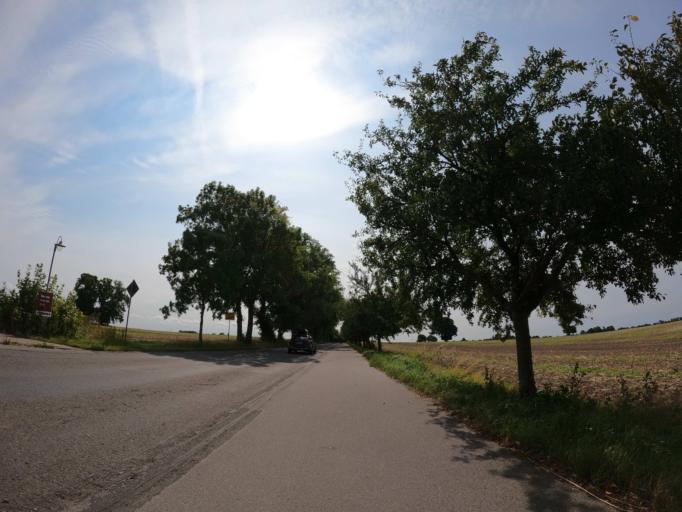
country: DE
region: Mecklenburg-Vorpommern
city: Kramerhof
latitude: 54.3483
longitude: 13.0691
